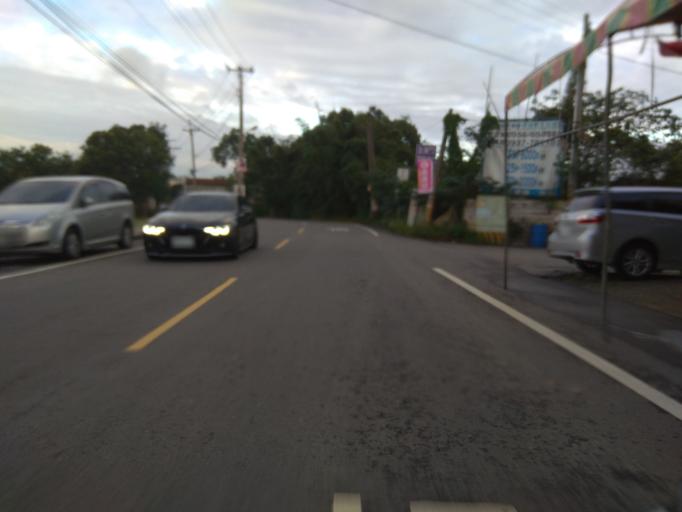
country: TW
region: Taiwan
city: Taoyuan City
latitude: 24.9497
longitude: 121.1923
